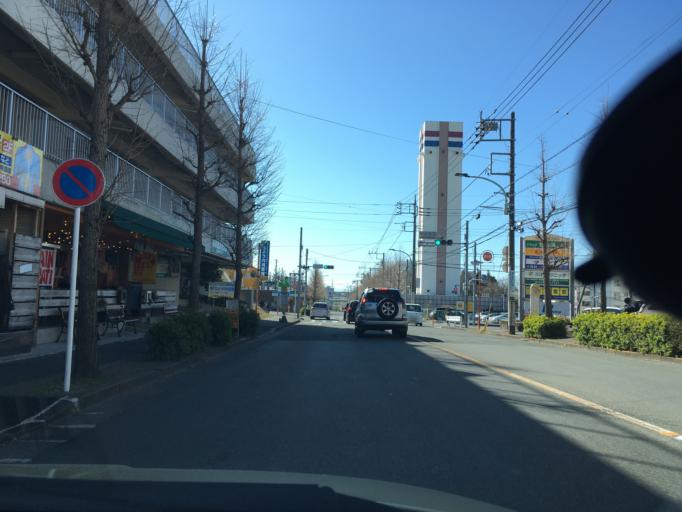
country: JP
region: Tokyo
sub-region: Machida-shi
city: Machida
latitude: 35.5711
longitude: 139.4389
